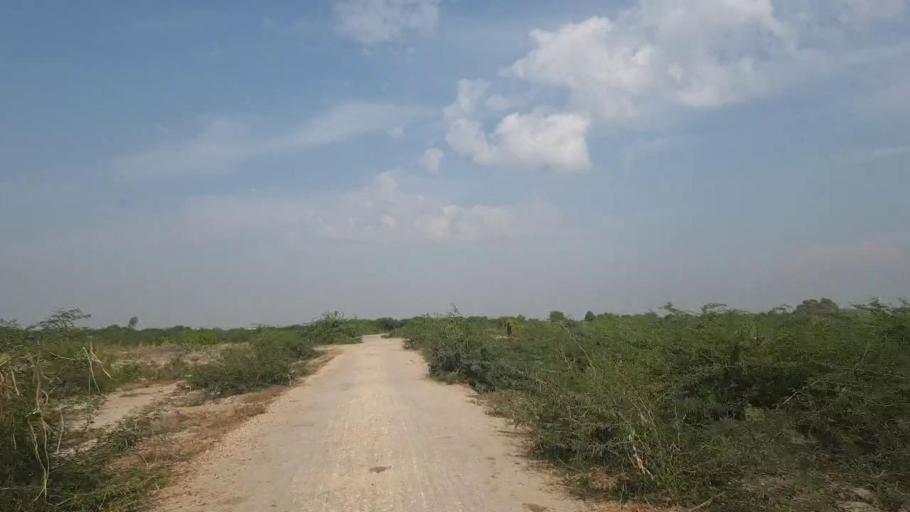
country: PK
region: Sindh
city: Digri
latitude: 25.0008
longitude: 69.0626
